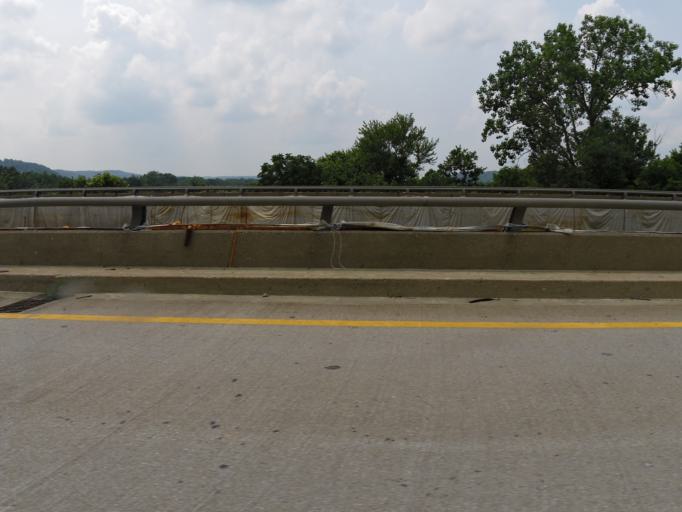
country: US
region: Kentucky
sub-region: Carroll County
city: Carrollton
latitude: 38.6437
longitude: -85.1241
